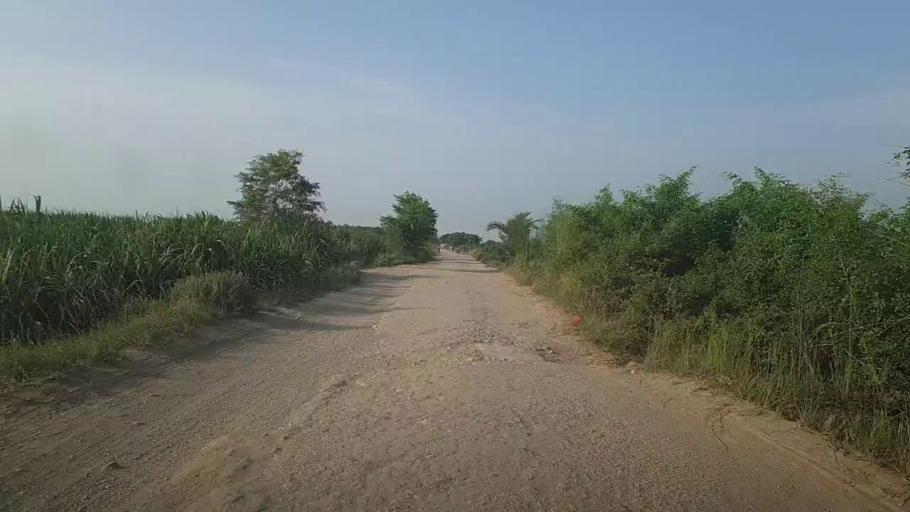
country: PK
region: Sindh
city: Ubauro
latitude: 28.3216
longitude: 69.7953
